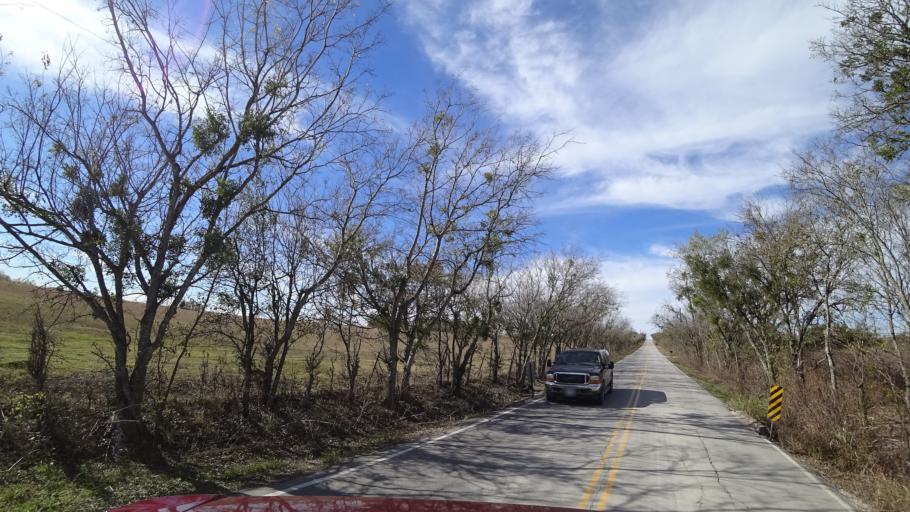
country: US
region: Texas
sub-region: Travis County
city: Onion Creek
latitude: 30.1044
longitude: -97.7344
